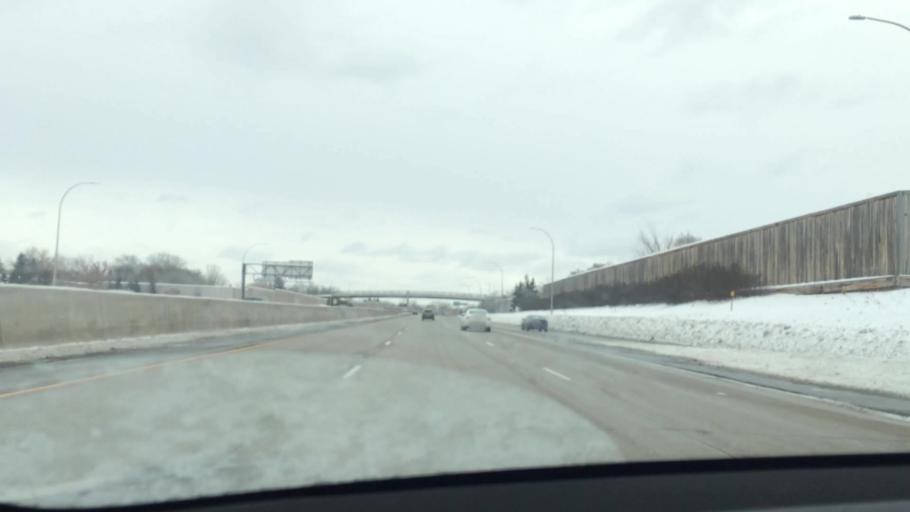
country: US
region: Minnesota
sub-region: Hennepin County
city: Robbinsdale
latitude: 45.0290
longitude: -93.3462
